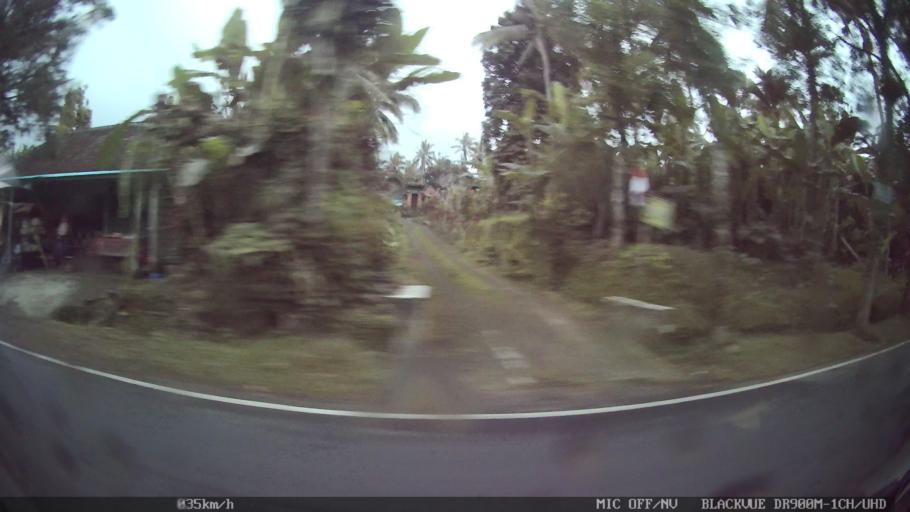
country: ID
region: Bali
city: Banjar Buahan
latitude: -8.3986
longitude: 115.2495
